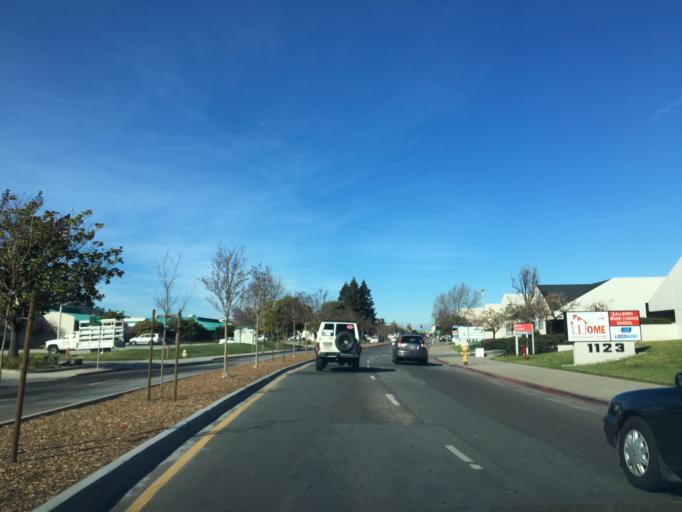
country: US
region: California
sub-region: San Mateo County
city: San Carlos
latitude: 37.5021
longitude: -122.2468
